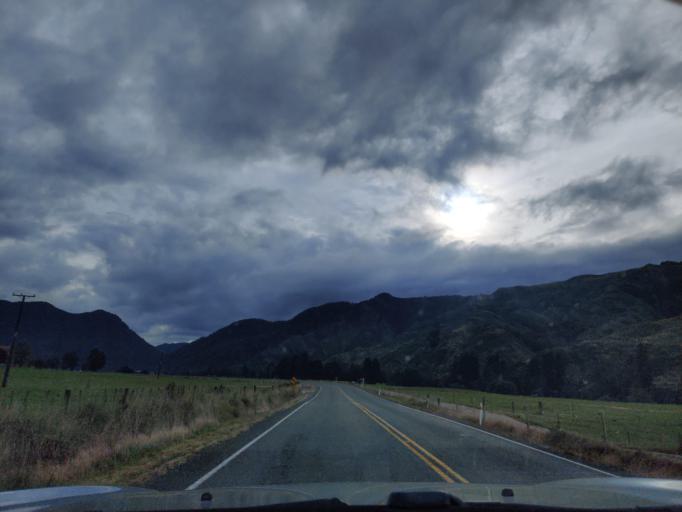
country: NZ
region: Tasman
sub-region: Tasman District
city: Wakefield
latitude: -41.7086
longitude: 172.4205
